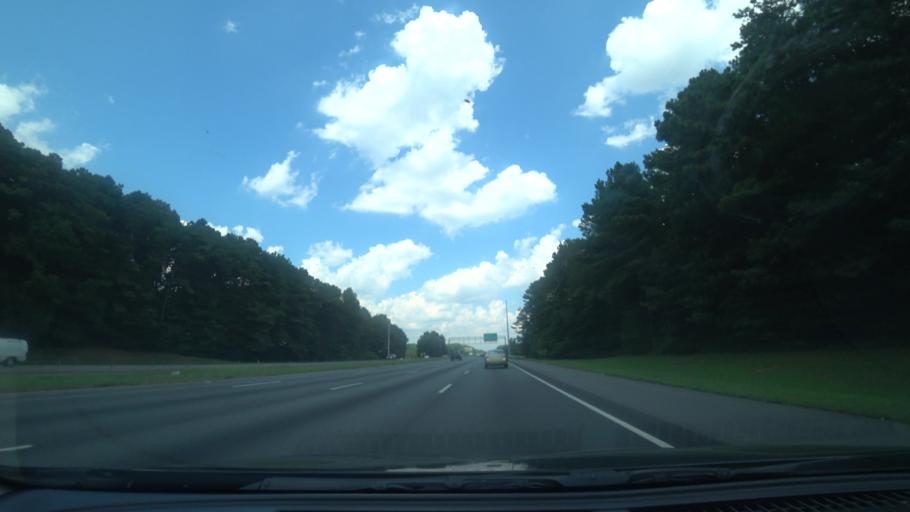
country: US
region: Georgia
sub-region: DeKalb County
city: Clarkston
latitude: 33.8229
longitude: -84.2379
